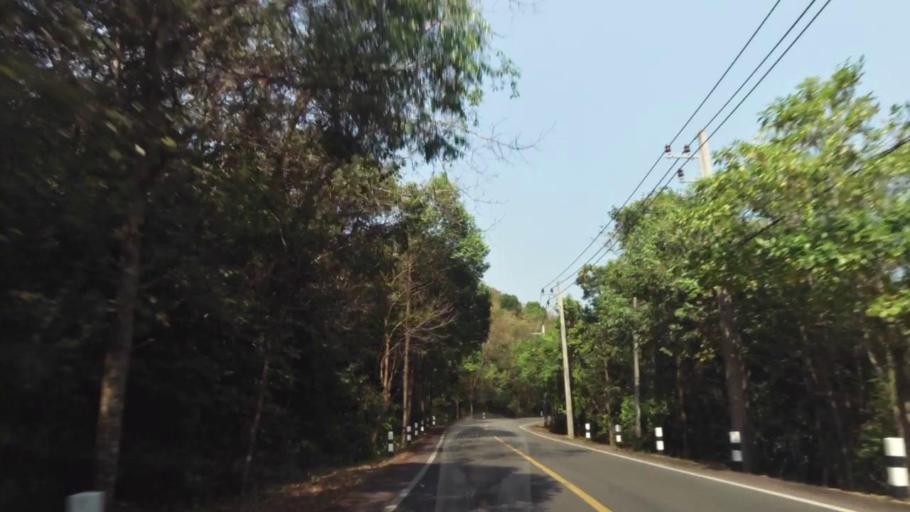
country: TH
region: Chanthaburi
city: Tha Mai
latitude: 12.5355
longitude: 101.9474
